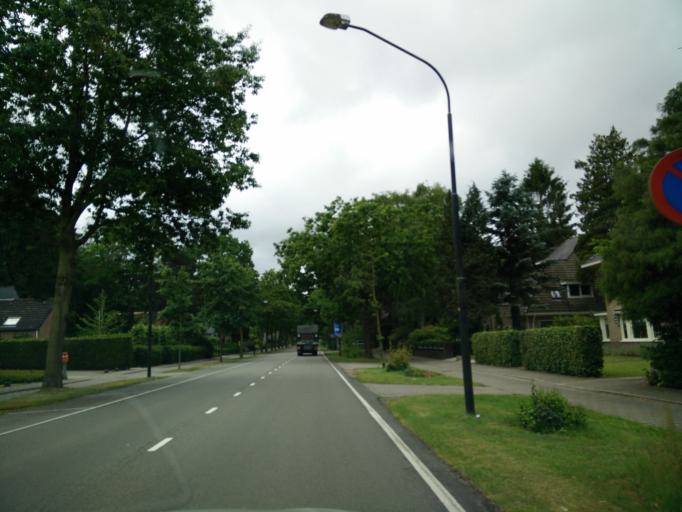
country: NL
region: Gelderland
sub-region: Gemeente Apeldoorn
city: Apeldoorn
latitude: 52.2136
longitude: 5.9323
